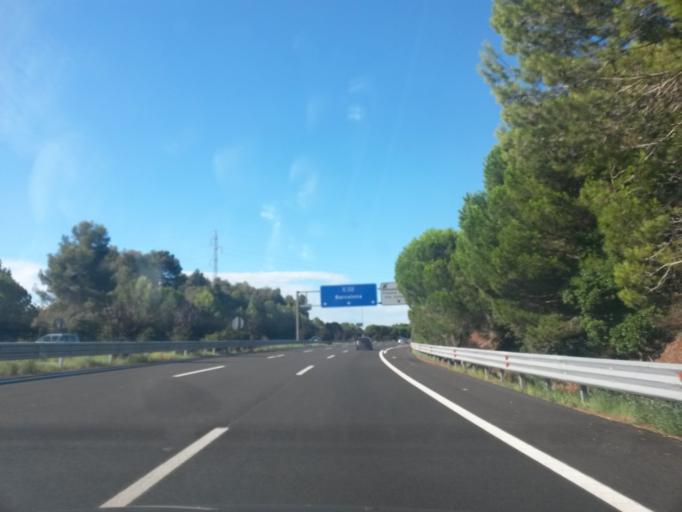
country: ES
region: Catalonia
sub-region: Provincia de Barcelona
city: Pineda de Mar
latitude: 41.6413
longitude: 2.6760
